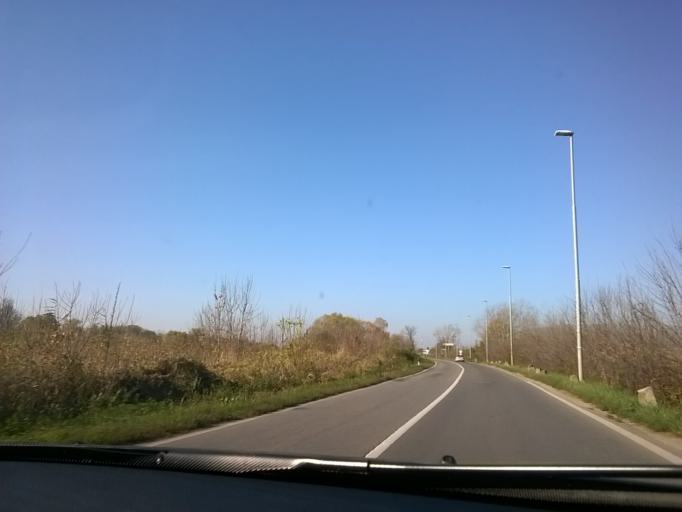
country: RS
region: Autonomna Pokrajina Vojvodina
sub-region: Juznobanatski Okrug
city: Pancevo
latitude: 44.8697
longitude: 20.6186
